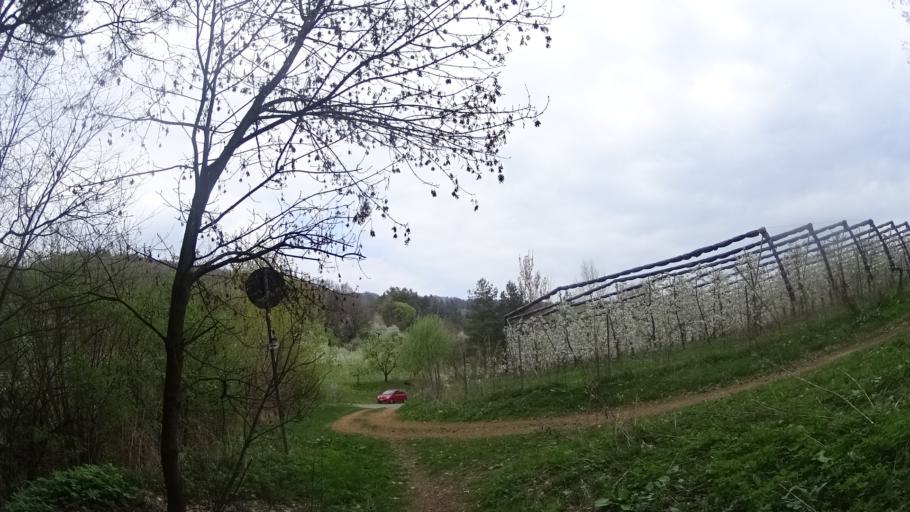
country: DE
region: Bavaria
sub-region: Upper Franconia
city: Kleinsendelbach
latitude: 49.6205
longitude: 11.1821
